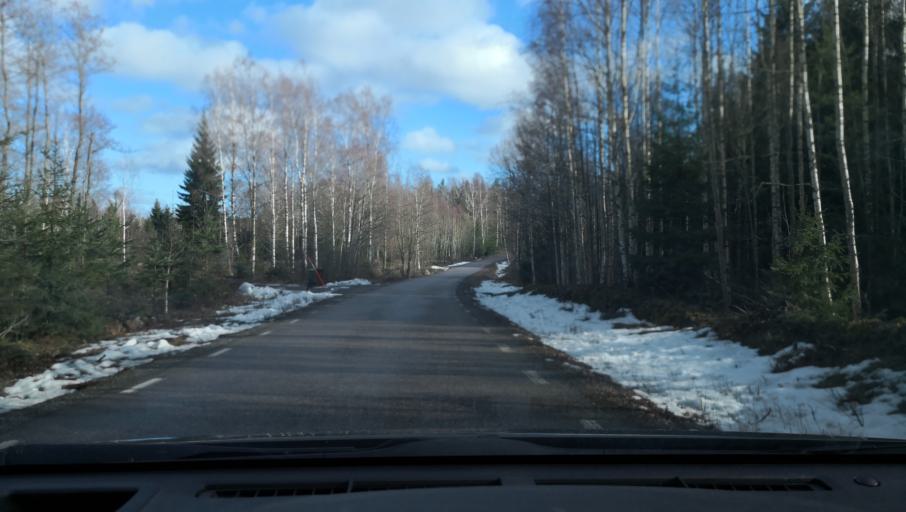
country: SE
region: Vaestmanland
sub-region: Arboga Kommun
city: Arboga
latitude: 59.3282
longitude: 15.7529
